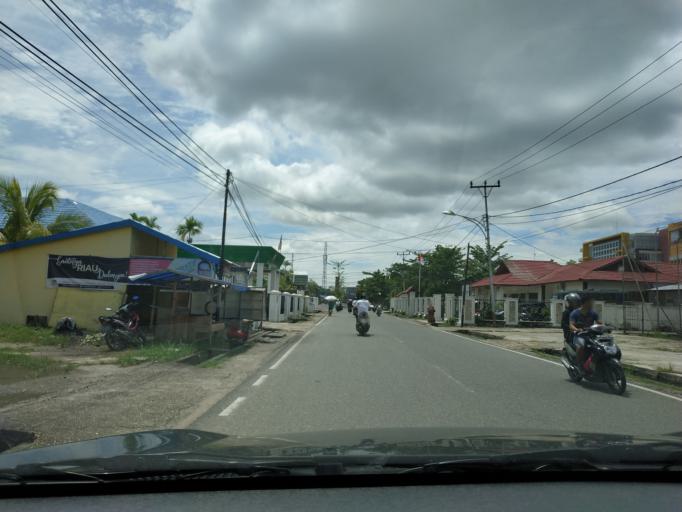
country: ID
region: Riau
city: Tembilahan
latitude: -0.3203
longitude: 103.1634
